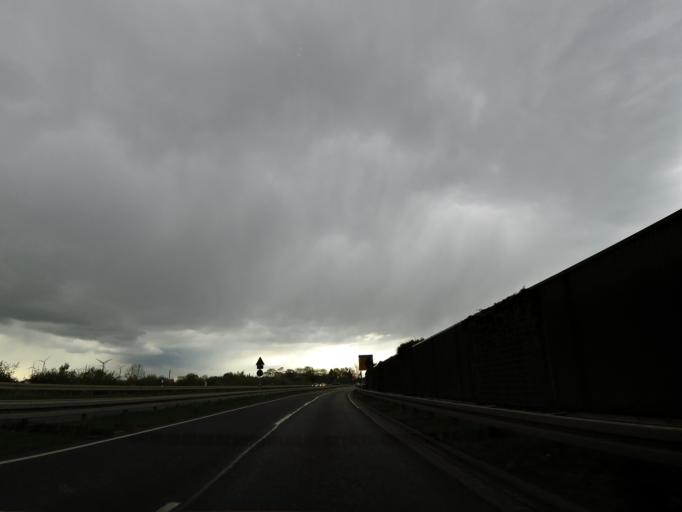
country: DE
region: Saxony-Anhalt
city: Egeln
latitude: 51.9500
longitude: 11.4298
